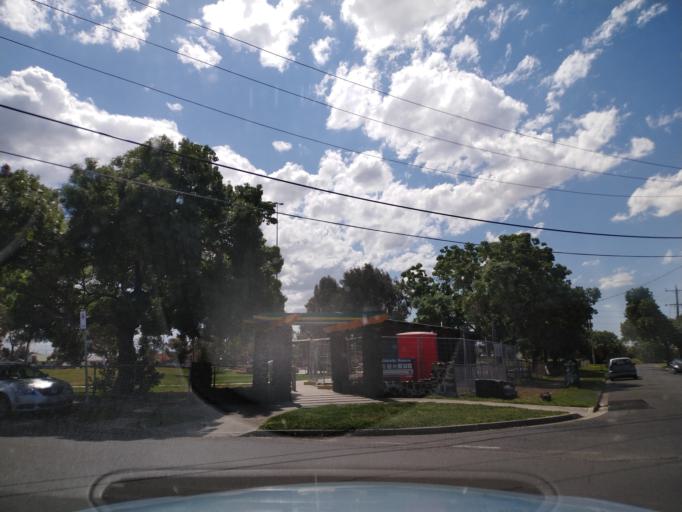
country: AU
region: Victoria
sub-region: Hobsons Bay
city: South Kingsville
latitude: -37.8287
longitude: 144.8710
